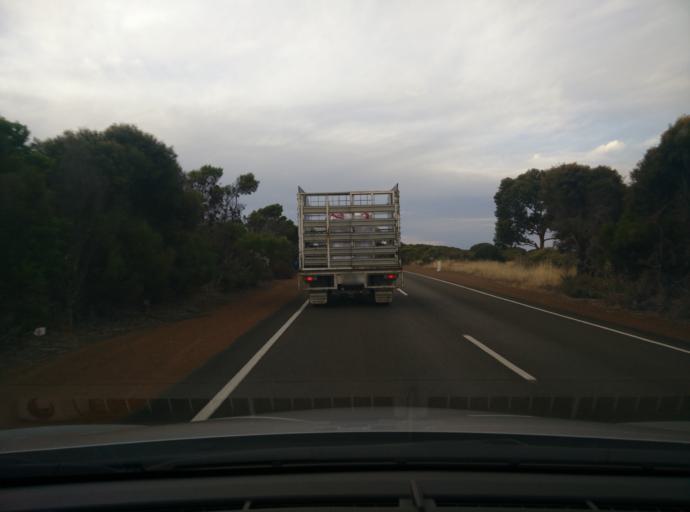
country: AU
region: South Australia
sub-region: Kangaroo Island
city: Kingscote
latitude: -35.7451
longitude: 137.5864
